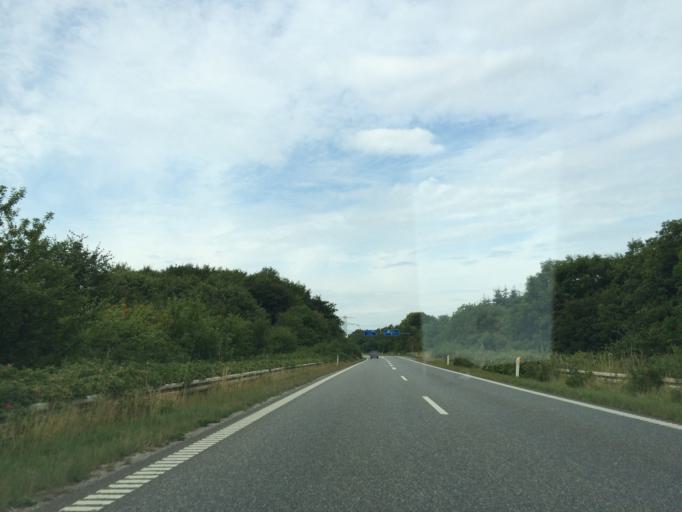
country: DK
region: South Denmark
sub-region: Kolding Kommune
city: Kolding
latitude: 55.5361
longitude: 9.5031
